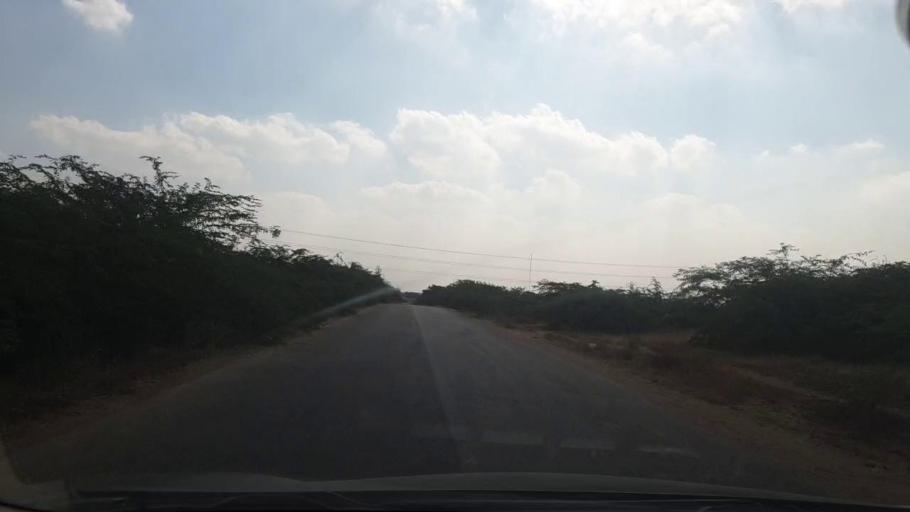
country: PK
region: Sindh
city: Malir Cantonment
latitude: 25.0121
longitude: 67.3536
